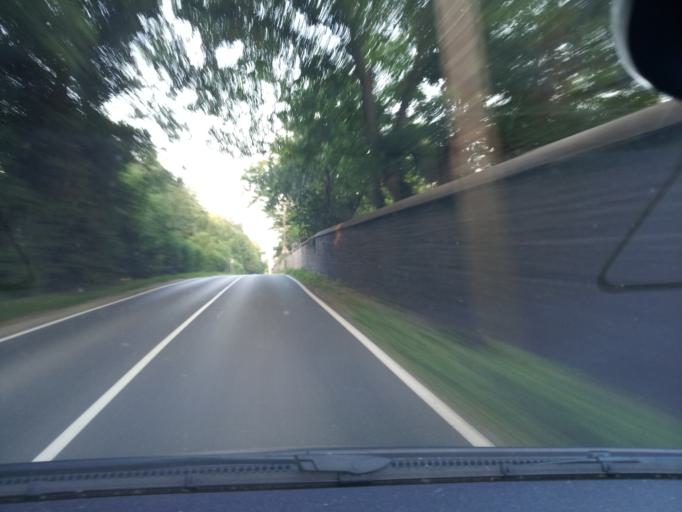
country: FR
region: Ile-de-France
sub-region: Departement de l'Essonne
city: Vert-le-Petit
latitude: 48.5403
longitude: 2.3580
